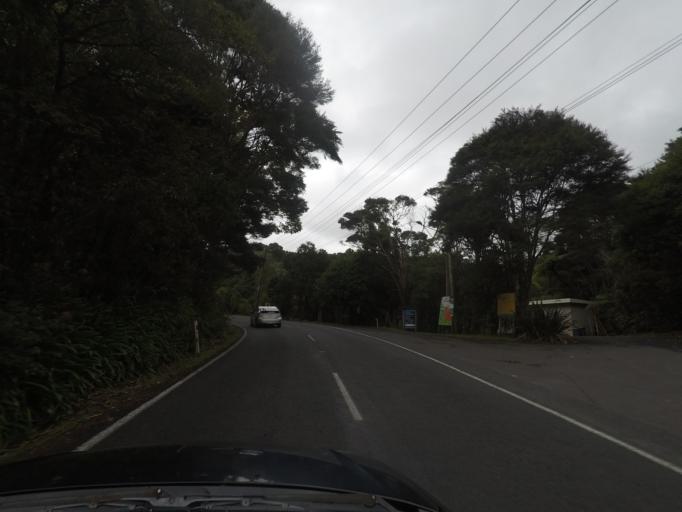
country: NZ
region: Auckland
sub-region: Auckland
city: Titirangi
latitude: -36.9311
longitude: 174.5807
